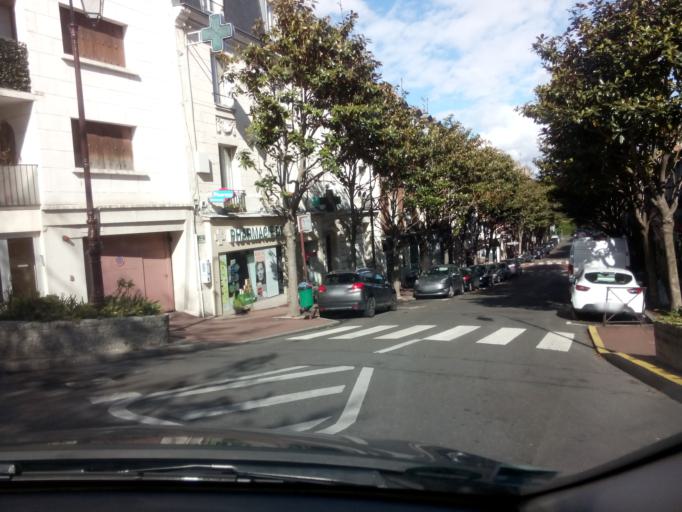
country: FR
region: Ile-de-France
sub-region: Departement des Hauts-de-Seine
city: Suresnes
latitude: 48.8567
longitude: 2.2211
